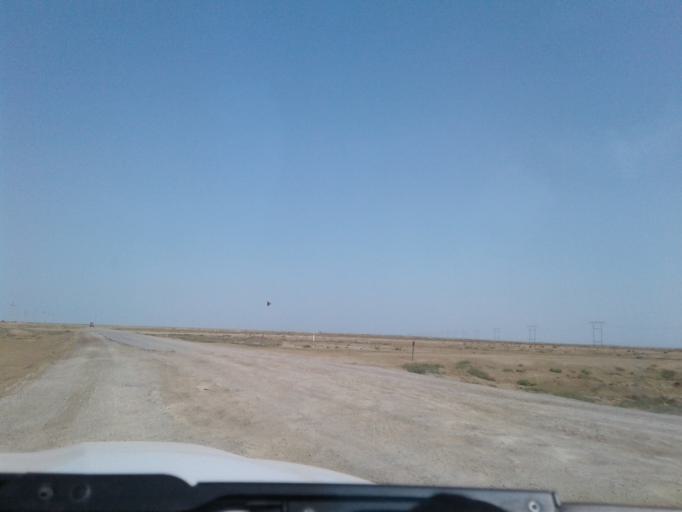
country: IR
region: Golestan
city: Gomishan
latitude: 37.7724
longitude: 53.9182
